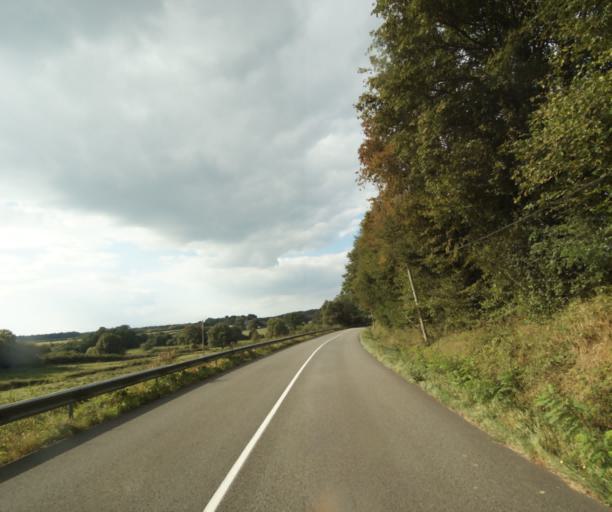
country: FR
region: Bourgogne
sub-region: Departement de Saone-et-Loire
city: Palinges
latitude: 46.5142
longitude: 4.2562
